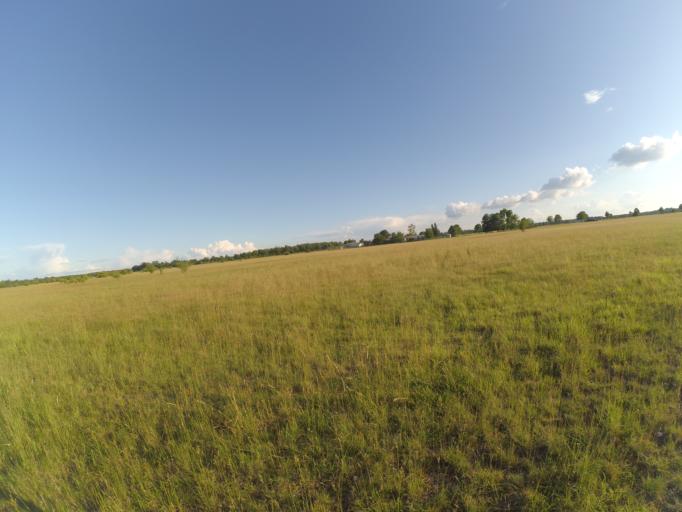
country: DE
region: Bavaria
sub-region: Upper Bavaria
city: Oberschleissheim
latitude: 48.2441
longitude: 11.5708
